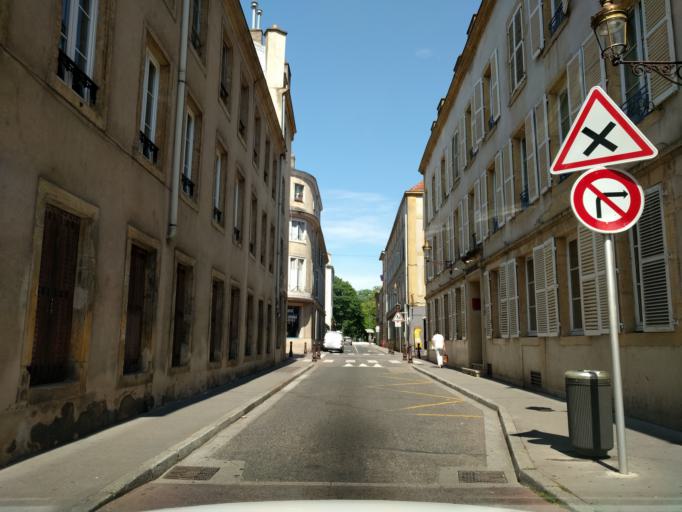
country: FR
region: Lorraine
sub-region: Departement de la Moselle
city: Metz
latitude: 49.1213
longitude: 6.1709
